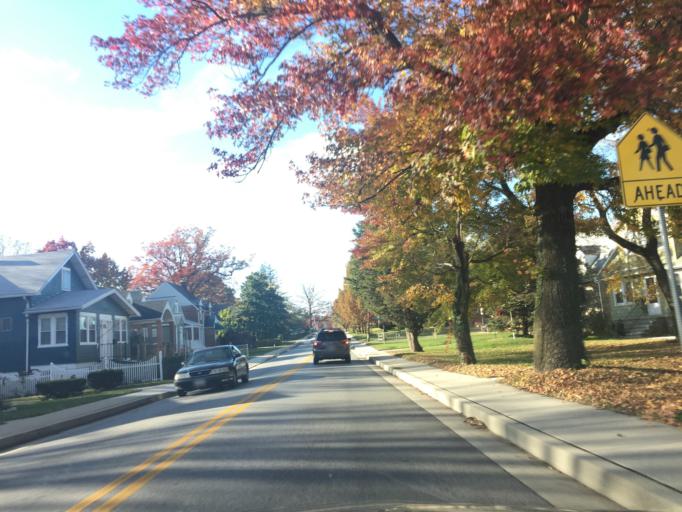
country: US
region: Maryland
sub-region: Baltimore County
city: Parkville
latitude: 39.3766
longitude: -76.5485
